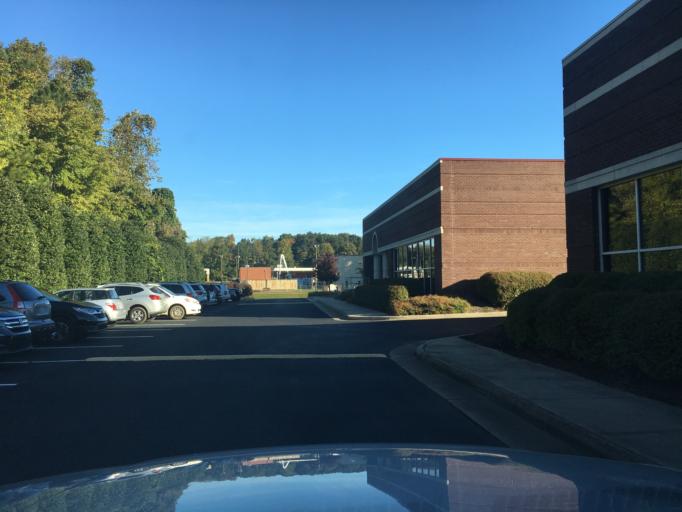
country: US
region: North Carolina
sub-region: Catawba County
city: Hickory
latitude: 35.7310
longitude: -81.3194
